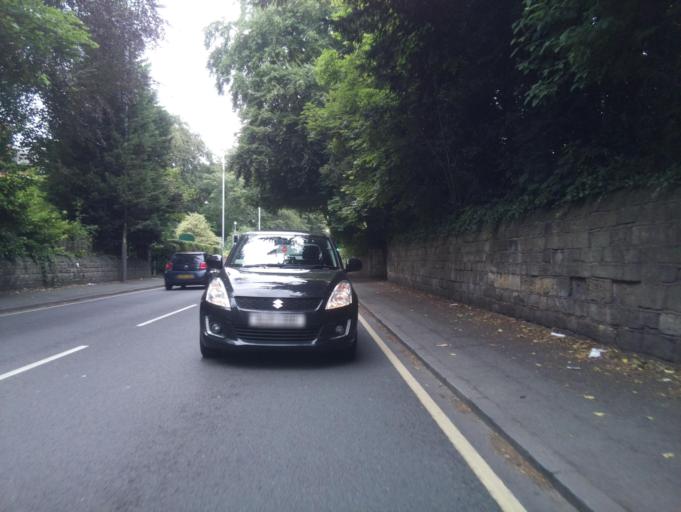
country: GB
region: England
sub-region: Wolverhampton
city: Wolverhampton
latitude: 52.5694
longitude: -2.1429
